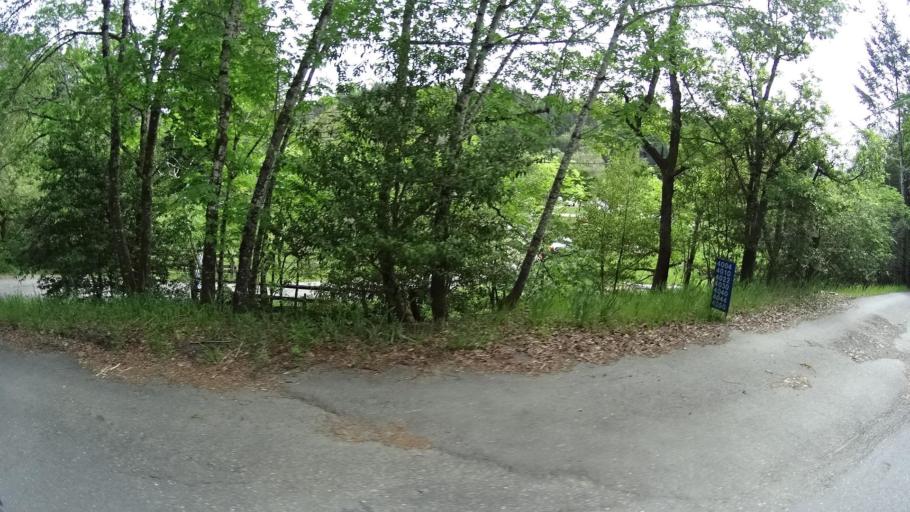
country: US
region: California
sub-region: Humboldt County
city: Redway
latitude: 40.0673
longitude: -123.8298
